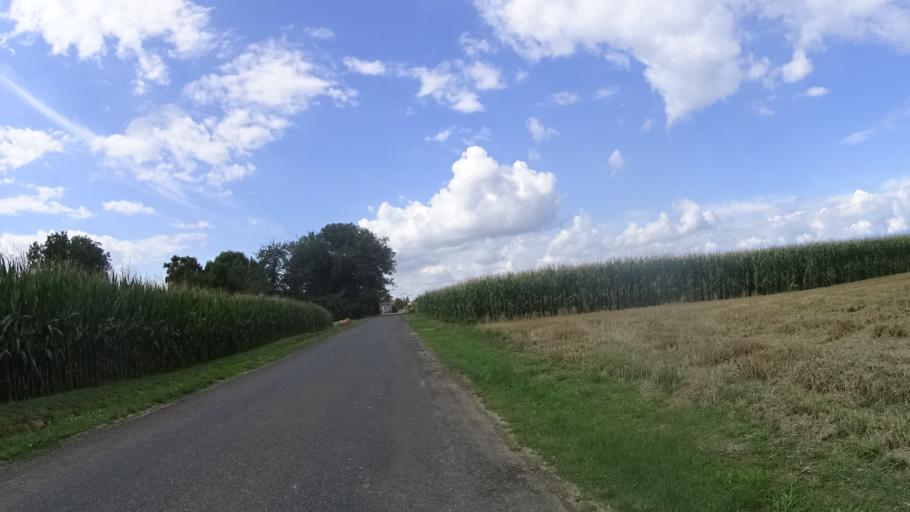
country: FR
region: Champagne-Ardenne
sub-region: Departement de la Marne
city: Pargny-sur-Saulx
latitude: 48.6885
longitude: 4.8063
